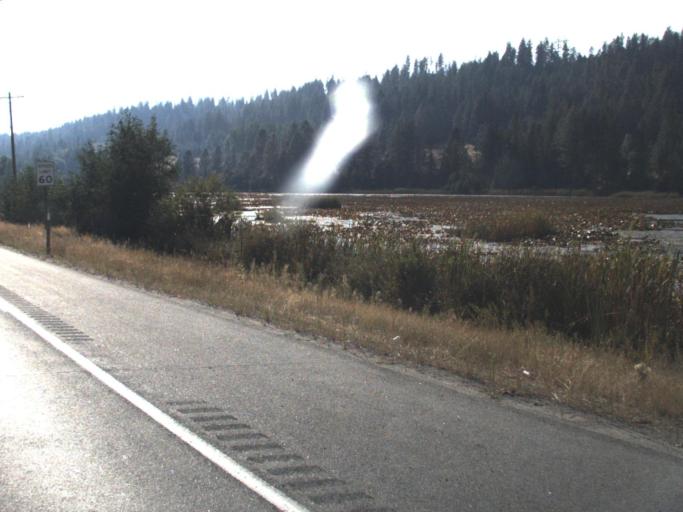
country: US
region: Washington
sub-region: Pend Oreille County
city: Newport
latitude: 48.1716
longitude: -117.0709
